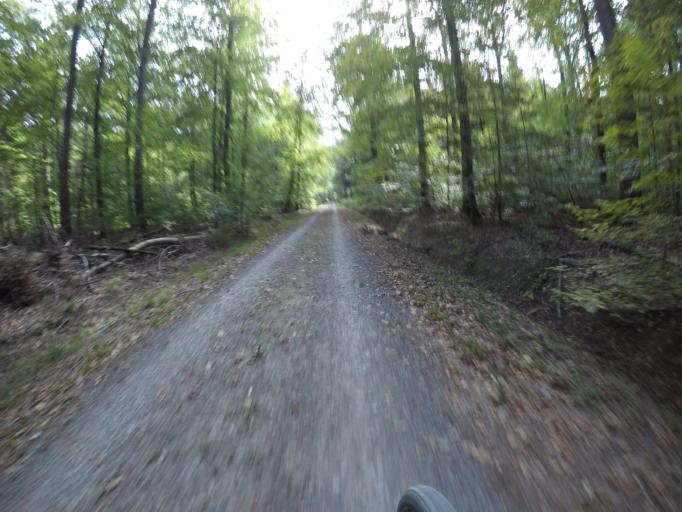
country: DE
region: Baden-Wuerttemberg
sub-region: Regierungsbezirk Stuttgart
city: Hildrizhausen
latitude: 48.6110
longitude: 8.9330
